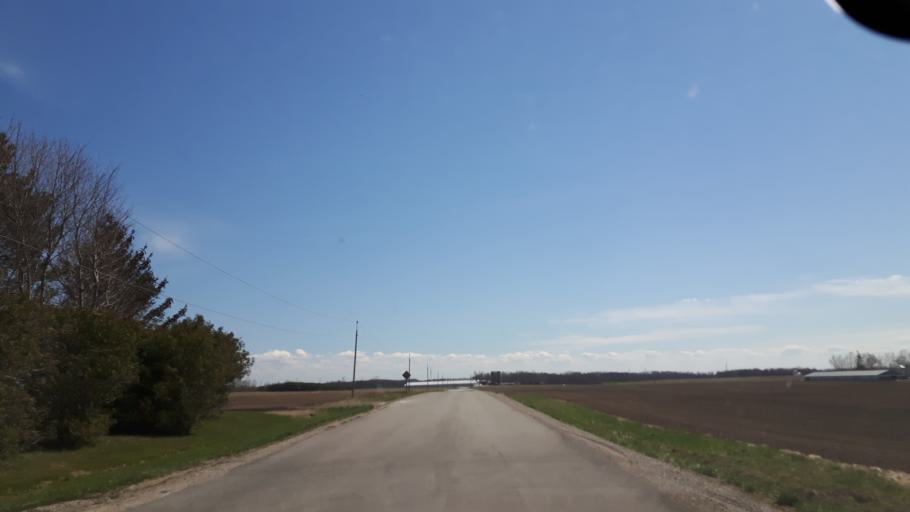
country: CA
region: Ontario
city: Bluewater
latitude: 43.5847
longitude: -81.6439
